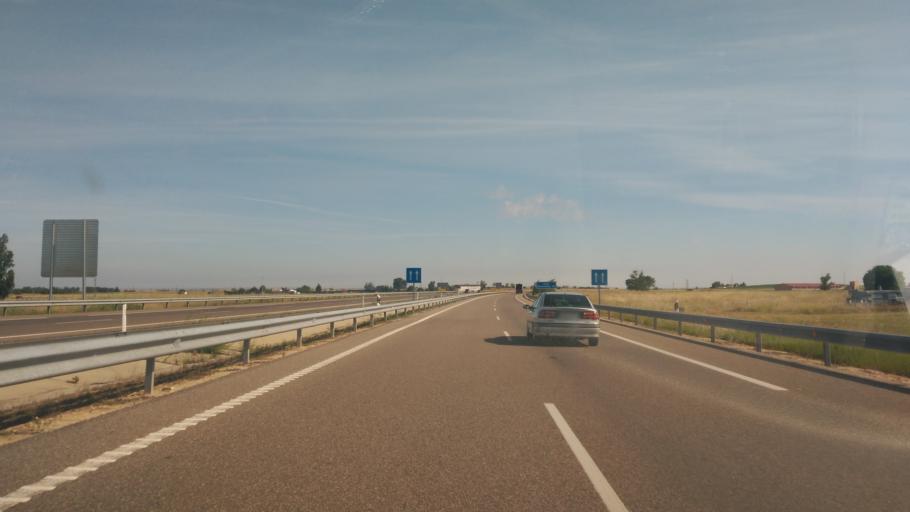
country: ES
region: Castille and Leon
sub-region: Provincia de Zamora
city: Cazurra
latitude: 41.4224
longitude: -5.7227
